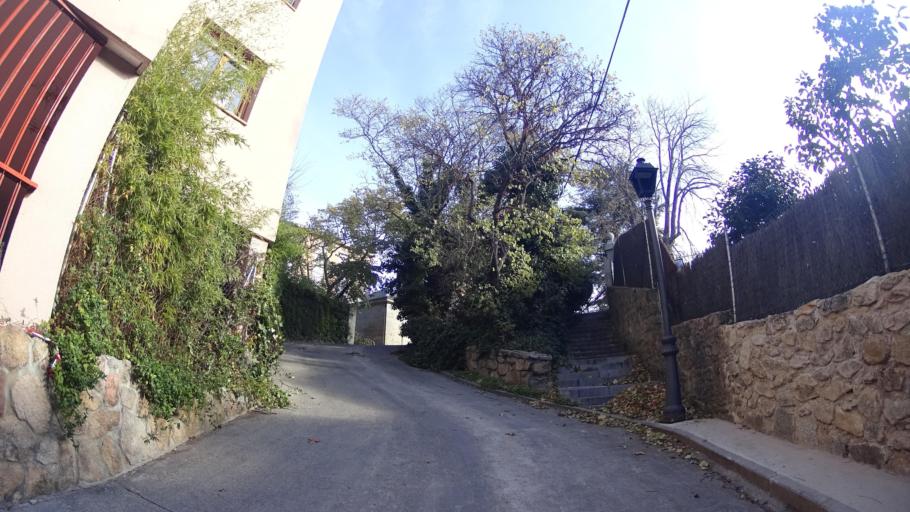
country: ES
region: Madrid
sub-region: Provincia de Madrid
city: San Lorenzo de El Escorial
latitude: 40.5884
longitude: -4.1535
